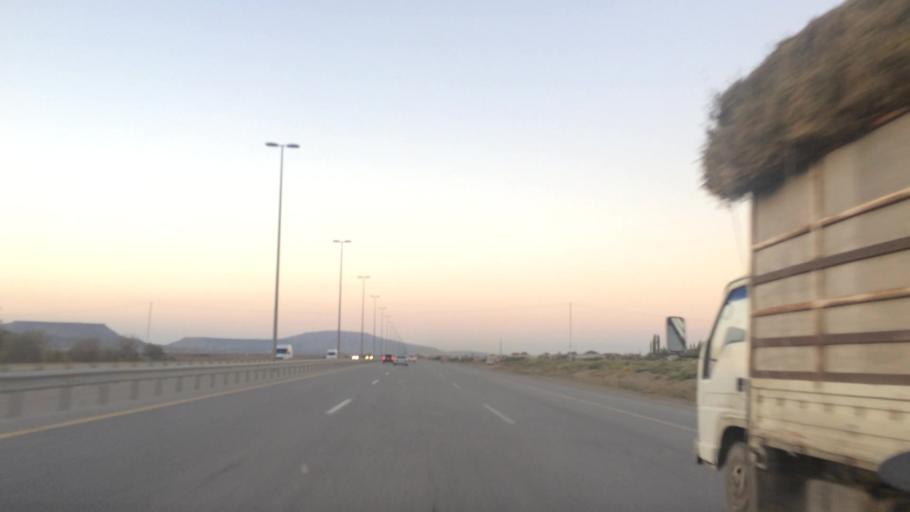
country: AZ
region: Baki
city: Qobustan
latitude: 40.0207
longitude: 49.4250
